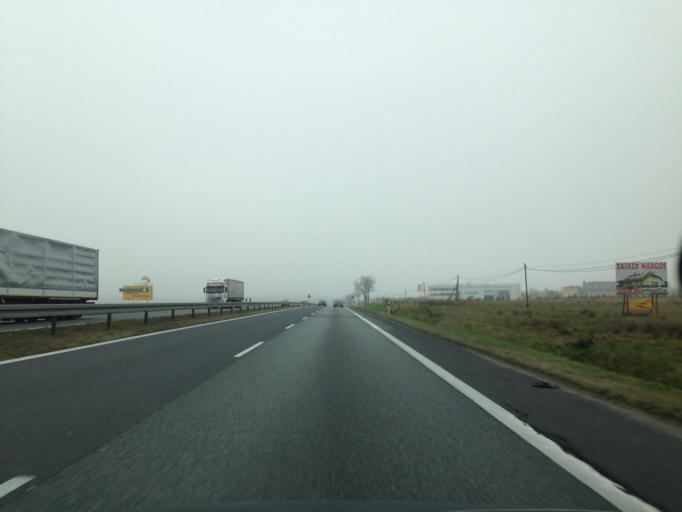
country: PL
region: Silesian Voivodeship
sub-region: Powiat myszkowski
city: Kozieglowy
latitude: 50.5578
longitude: 19.1765
